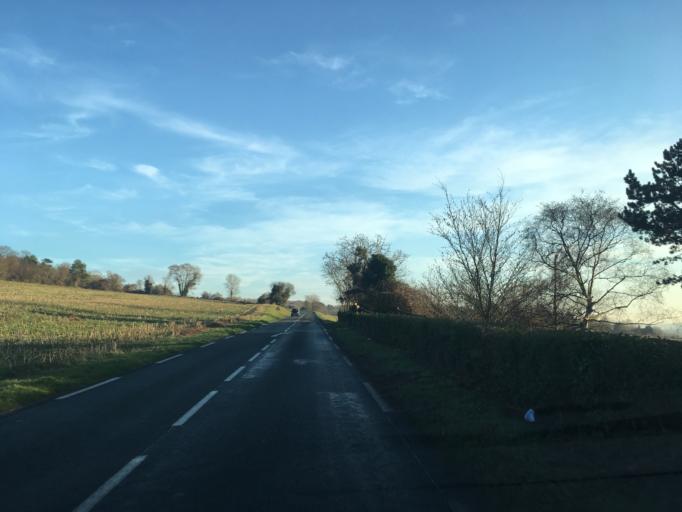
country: FR
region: Haute-Normandie
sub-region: Departement de l'Eure
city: Houlbec-Cocherel
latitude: 49.0567
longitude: 1.3375
